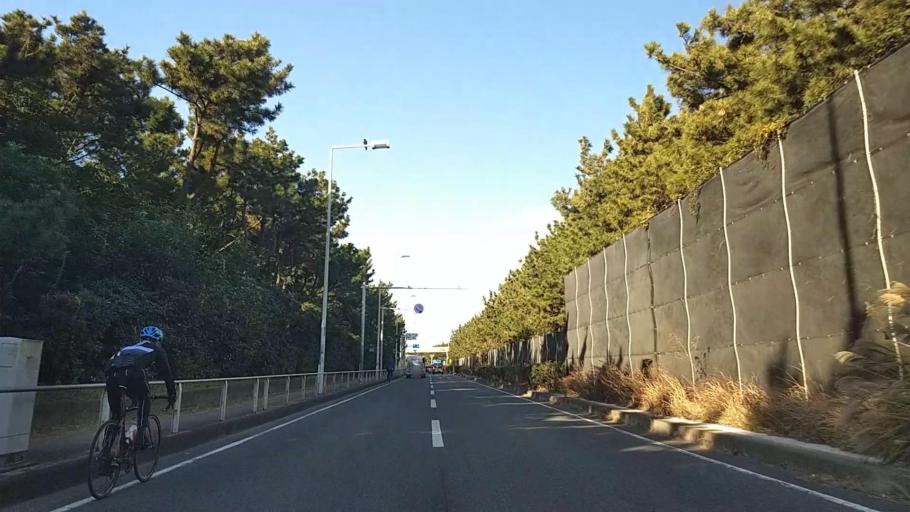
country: JP
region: Kanagawa
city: Fujisawa
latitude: 35.3200
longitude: 139.4465
